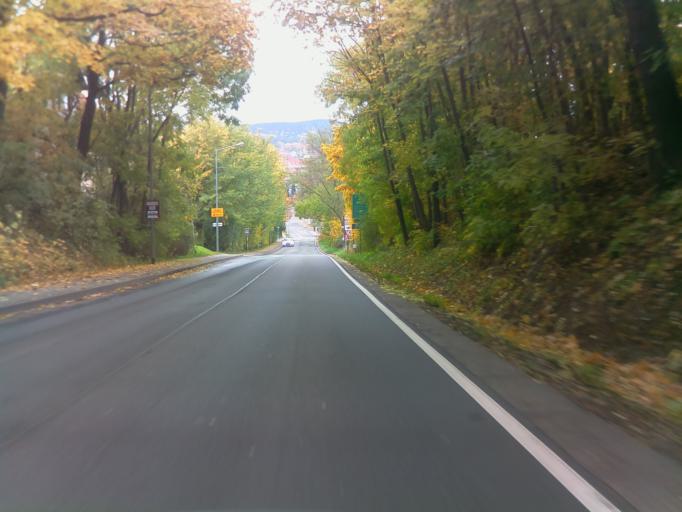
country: DE
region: Thuringia
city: Arnstadt
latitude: 50.8312
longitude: 10.9660
